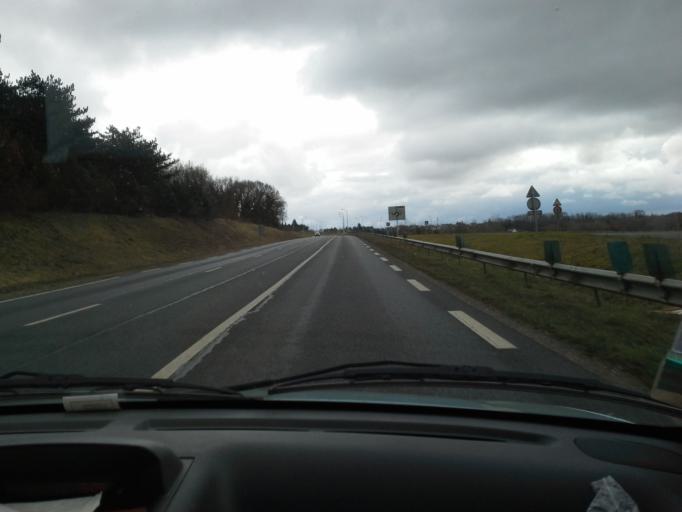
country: FR
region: Centre
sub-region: Departement du Loir-et-Cher
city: Saint-Sulpice-de-Pommeray
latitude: 47.6526
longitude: 1.2724
